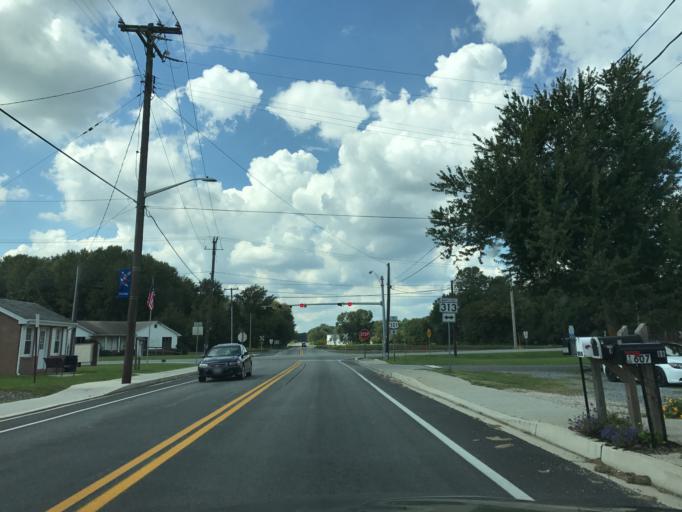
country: US
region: Maryland
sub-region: Caroline County
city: Greensboro
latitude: 39.1445
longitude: -75.8637
